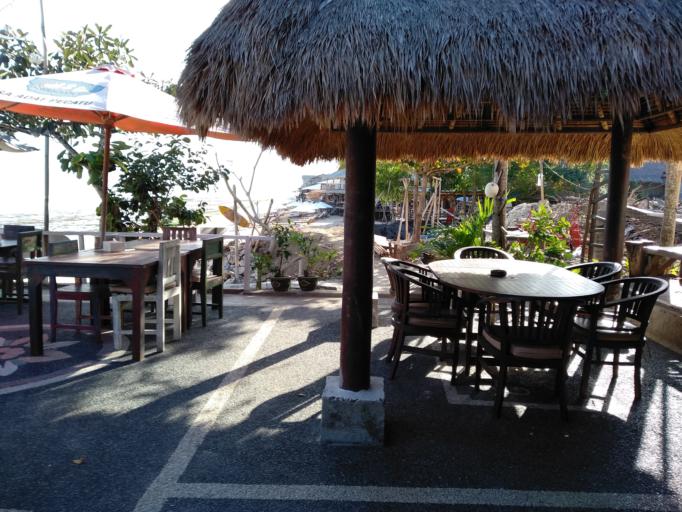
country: ID
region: Bali
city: Jimbaran
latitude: -8.7938
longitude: 115.1223
